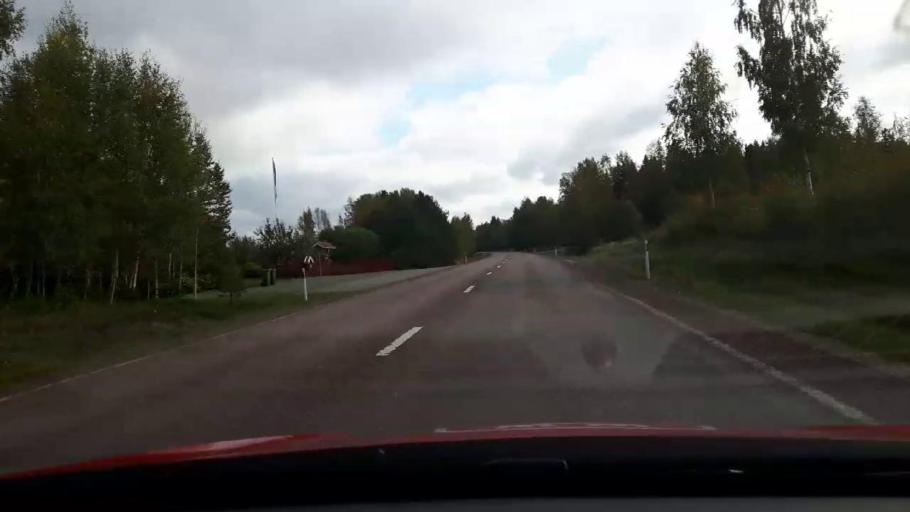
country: SE
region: Gaevleborg
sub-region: Ljusdals Kommun
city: Jaervsoe
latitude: 61.6467
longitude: 16.2022
